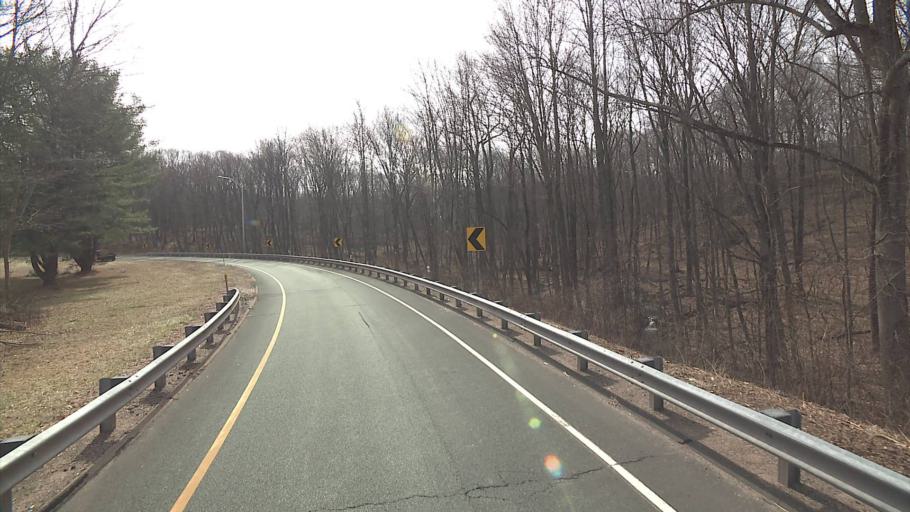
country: US
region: Connecticut
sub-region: Middlesex County
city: Higganum
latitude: 41.5133
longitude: -72.6014
